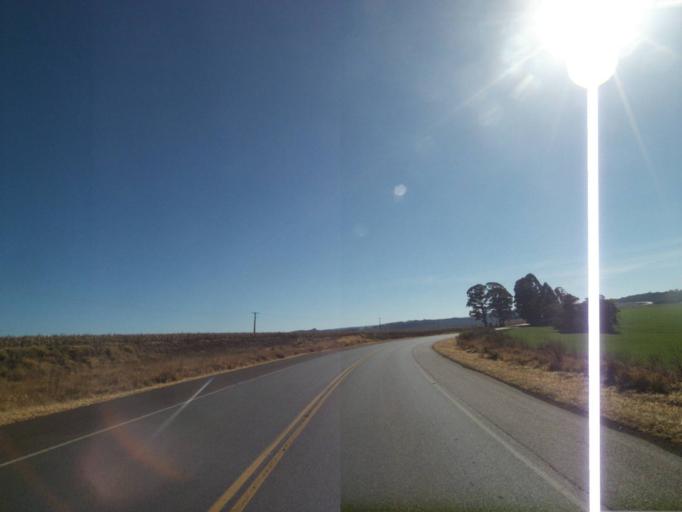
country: BR
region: Parana
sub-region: Tibagi
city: Tibagi
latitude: -24.3926
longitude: -50.3363
